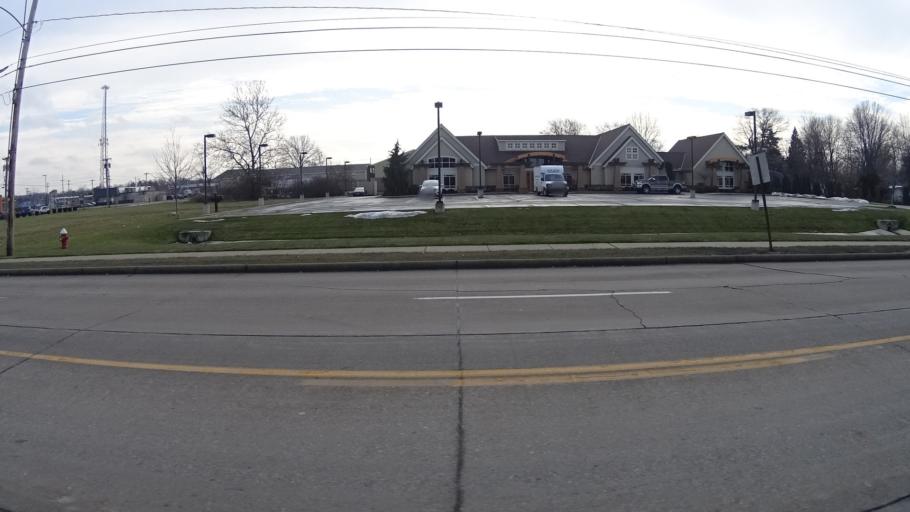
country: US
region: Ohio
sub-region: Lorain County
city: Amherst
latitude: 41.4183
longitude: -82.2107
